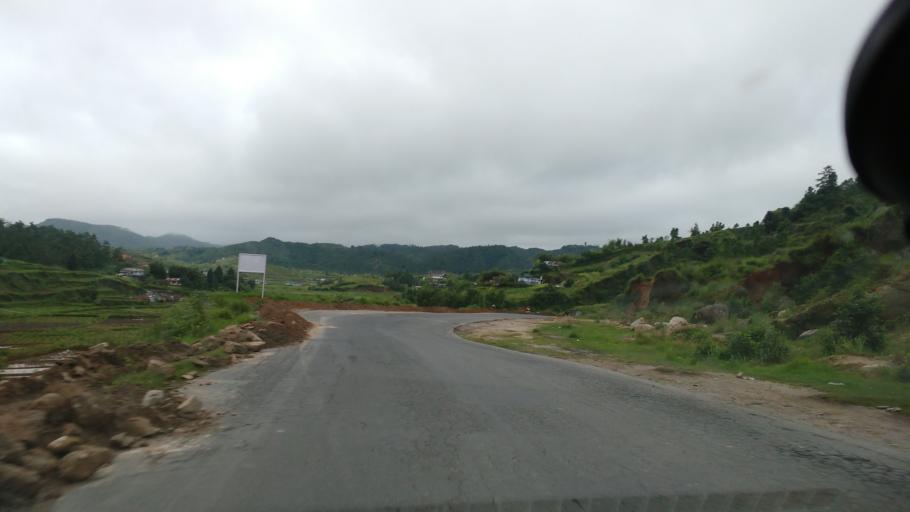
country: IN
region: Meghalaya
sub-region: East Khasi Hills
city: Shillong
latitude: 25.5160
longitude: 91.8123
